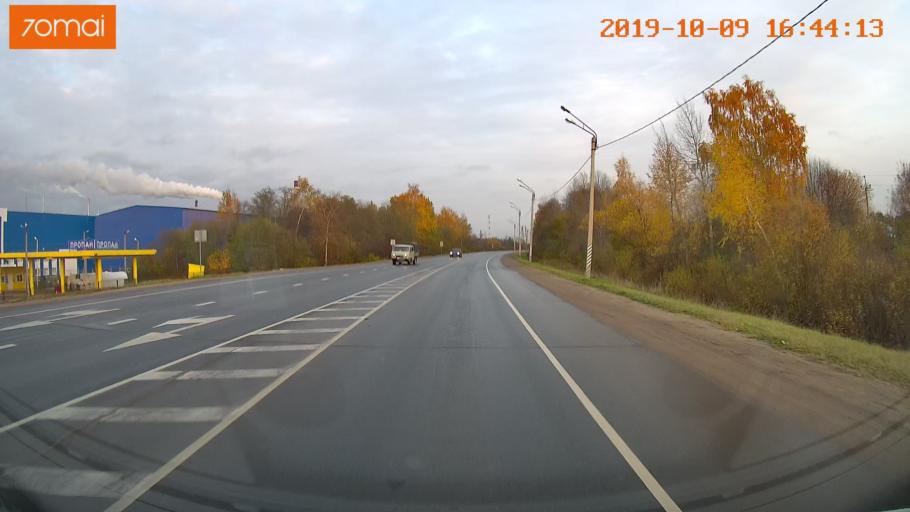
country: RU
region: Kostroma
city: Volgorechensk
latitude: 57.4521
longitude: 41.1376
